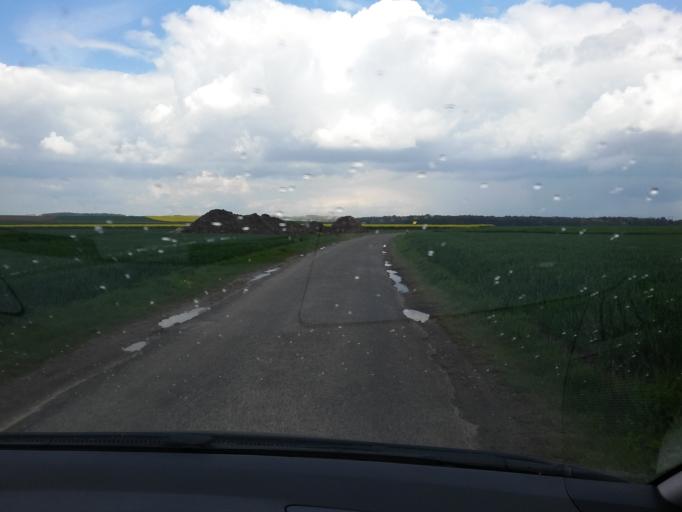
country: FR
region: Picardie
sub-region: Departement de l'Oise
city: Chevrieres
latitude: 49.3639
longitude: 2.6844
